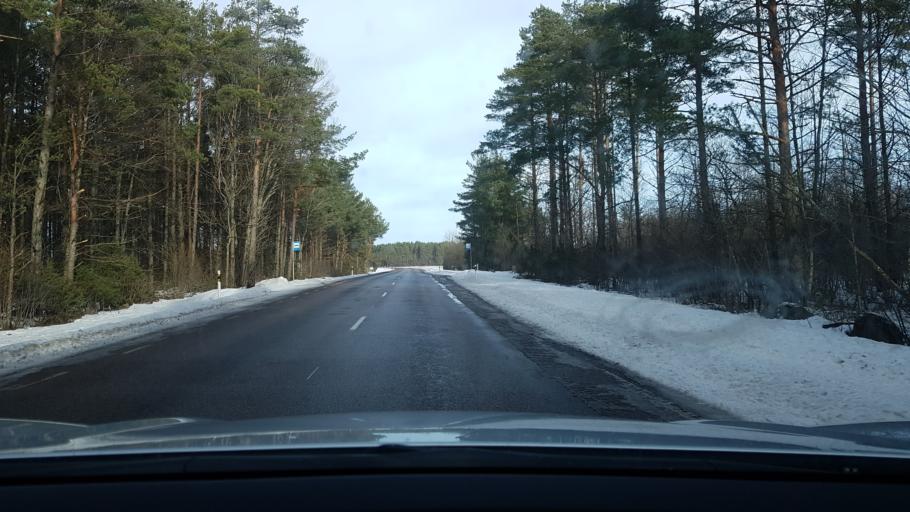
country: EE
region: Saare
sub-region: Kuressaare linn
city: Kuressaare
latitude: 58.3612
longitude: 22.6089
